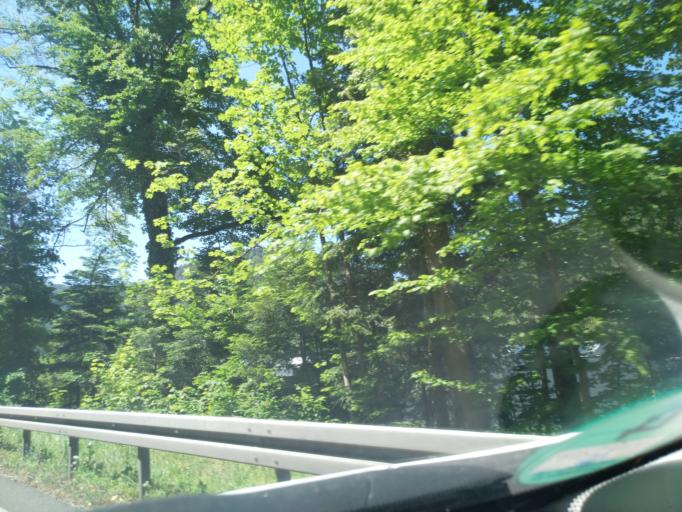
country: DE
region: Baden-Wuerttemberg
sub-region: Karlsruhe Region
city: Neuenburg
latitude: 48.8315
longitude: 8.5849
